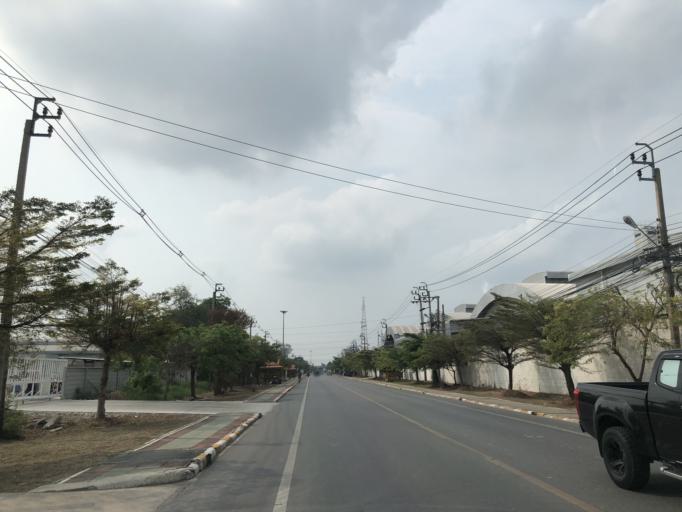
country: TH
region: Samut Prakan
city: Bang Bo District
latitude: 13.5901
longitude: 100.7427
